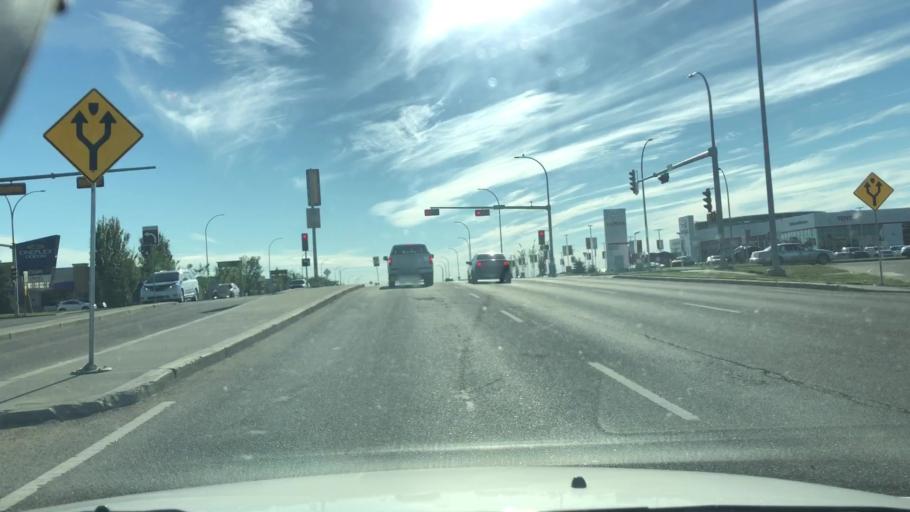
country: CA
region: Alberta
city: St. Albert
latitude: 53.5995
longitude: -113.5679
